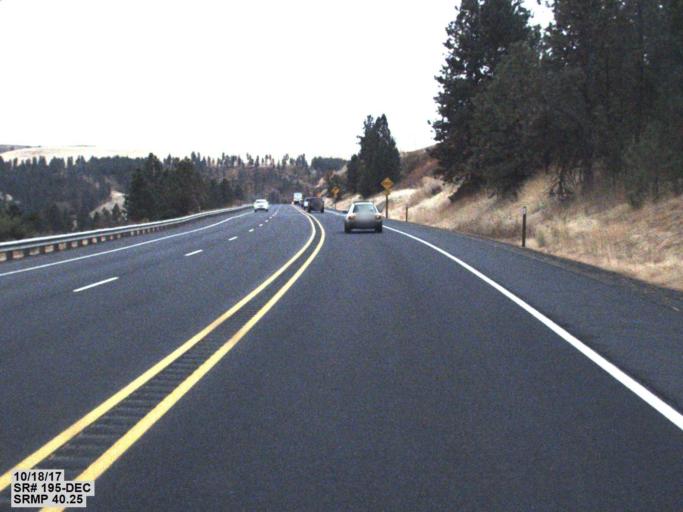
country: US
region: Washington
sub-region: Whitman County
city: Colfax
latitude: 46.9096
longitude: -117.3506
